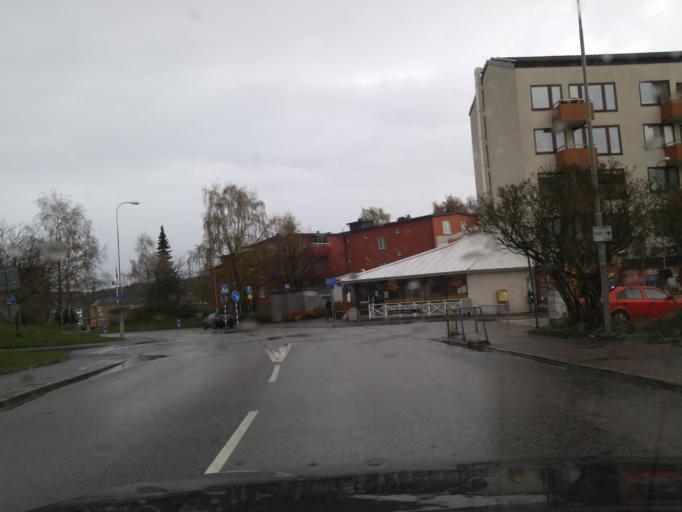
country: SE
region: Vaestra Goetaland
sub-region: Goteborg
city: Majorna
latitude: 57.6716
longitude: 11.9281
